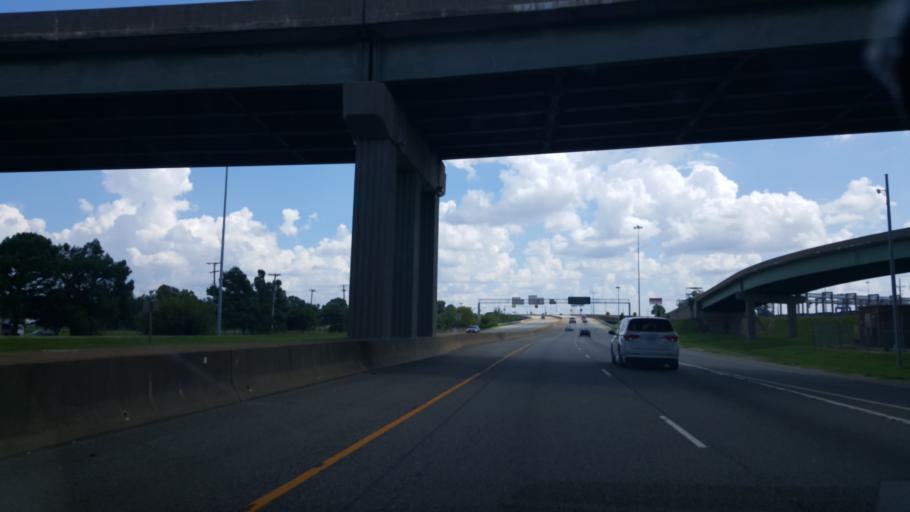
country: US
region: Virginia
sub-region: City of Newport News
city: Newport News
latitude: 36.9803
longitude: -76.4243
